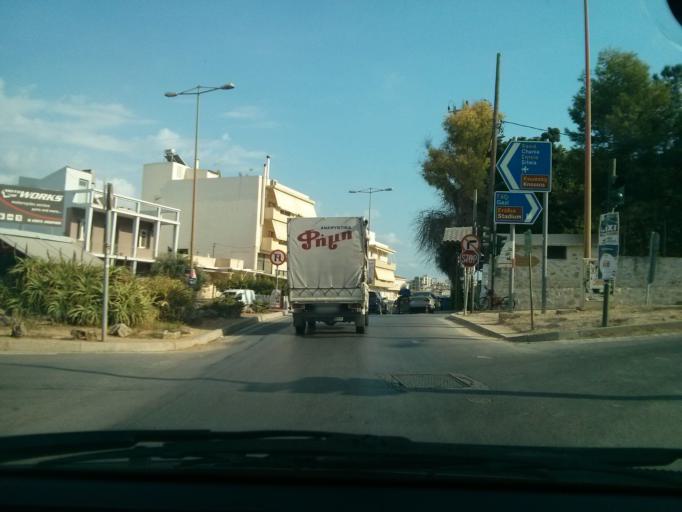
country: GR
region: Crete
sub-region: Nomos Irakleiou
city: Irakleion
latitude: 35.3286
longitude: 25.1376
